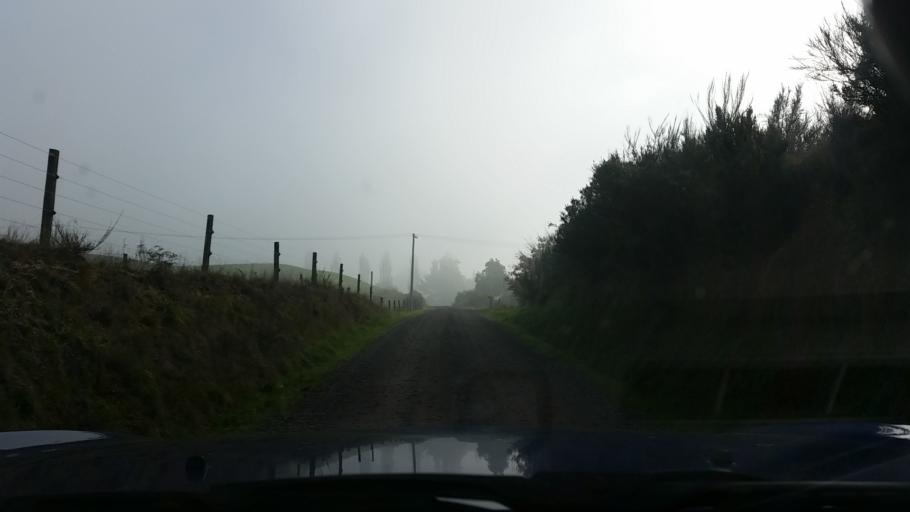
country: NZ
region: Bay of Plenty
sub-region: Rotorua District
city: Rotorua
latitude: -38.4444
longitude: 176.2850
